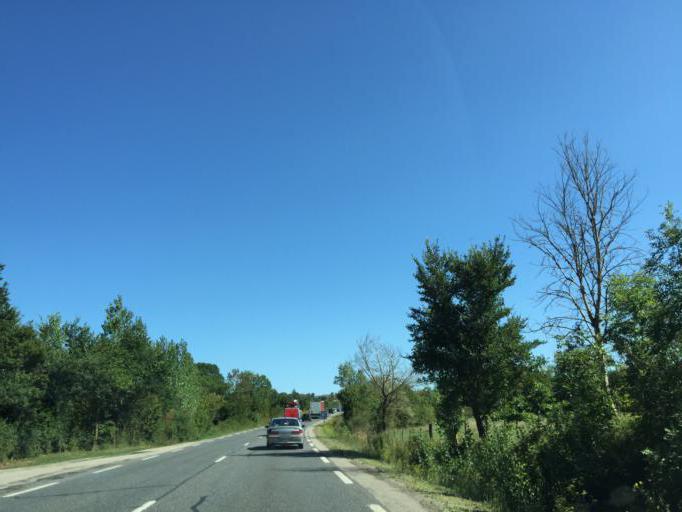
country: FR
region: Midi-Pyrenees
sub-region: Departement de l'Aveyron
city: Severac-le-Chateau
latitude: 44.3421
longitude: 3.0231
